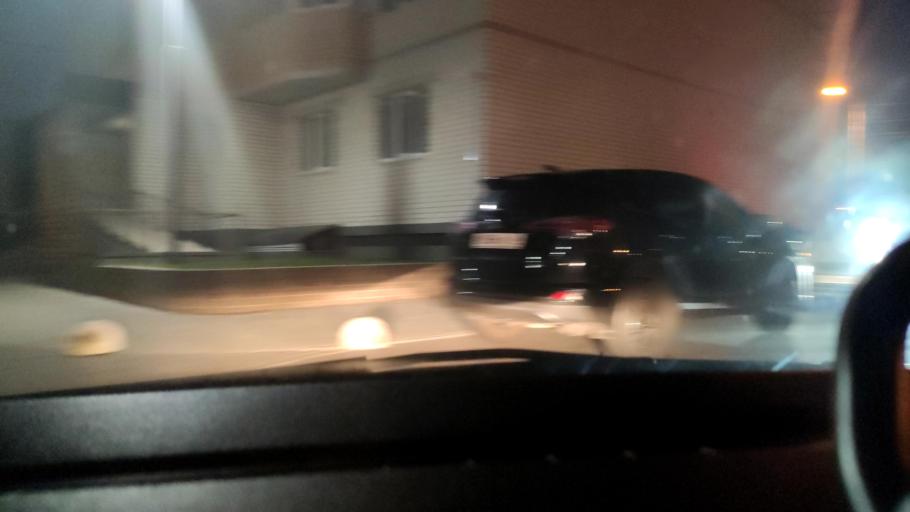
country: RU
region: Voronezj
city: Podgornoye
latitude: 51.7218
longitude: 39.1413
